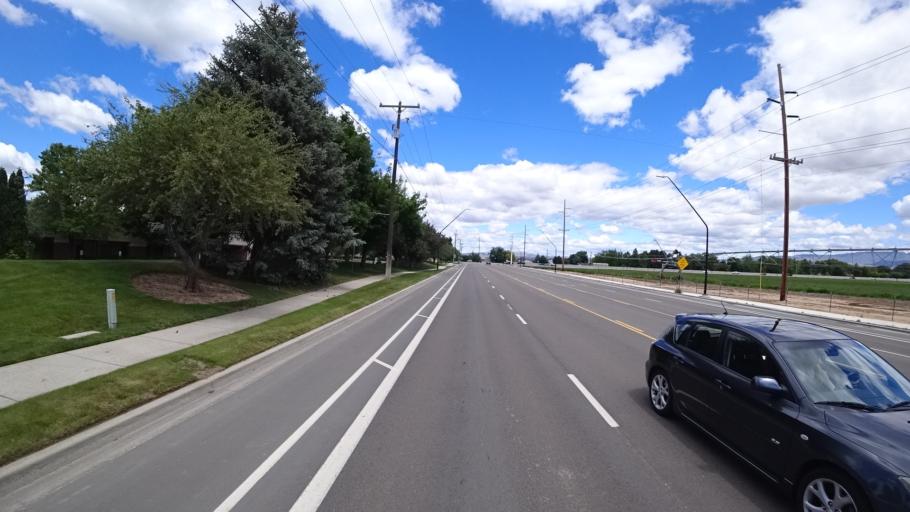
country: US
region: Idaho
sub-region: Ada County
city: Eagle
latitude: 43.6605
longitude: -116.3345
